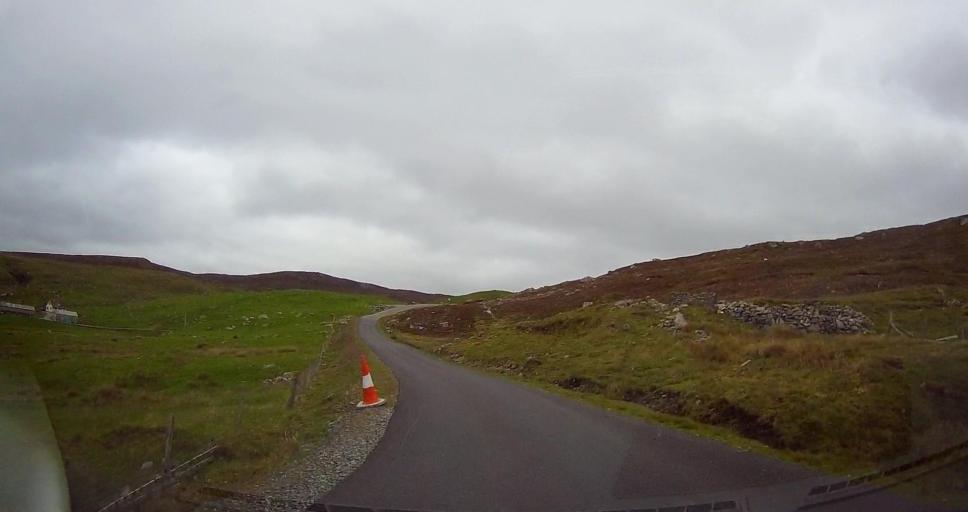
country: GB
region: Scotland
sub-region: Shetland Islands
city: Lerwick
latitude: 60.3354
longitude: -1.3276
